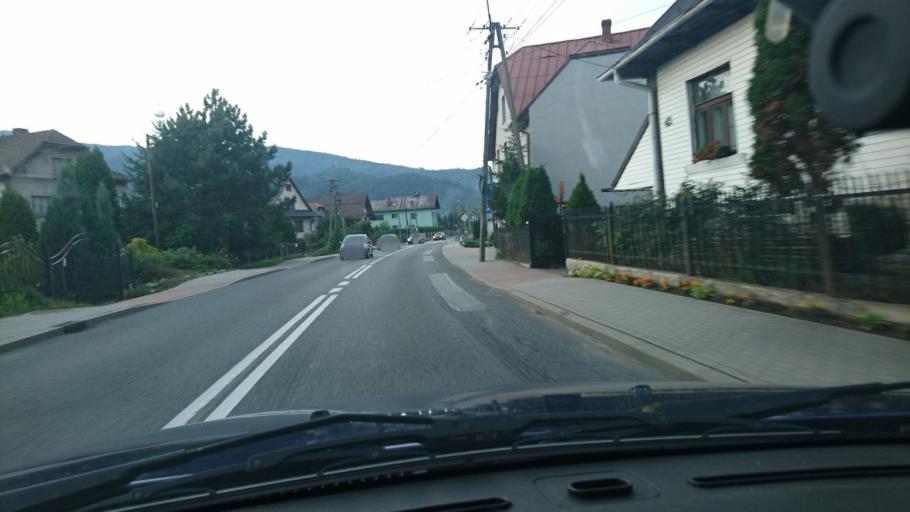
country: PL
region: Silesian Voivodeship
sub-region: Powiat zywiecki
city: Cisiec
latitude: 49.5954
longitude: 19.1073
